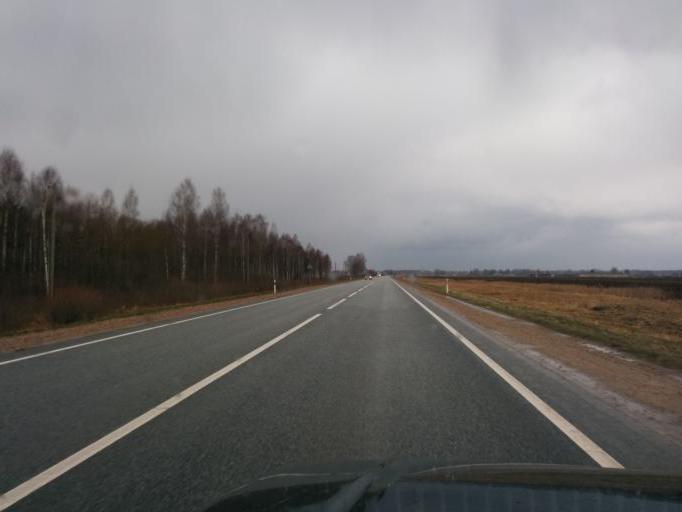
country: LV
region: Marupe
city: Marupe
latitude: 56.8604
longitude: 23.9874
